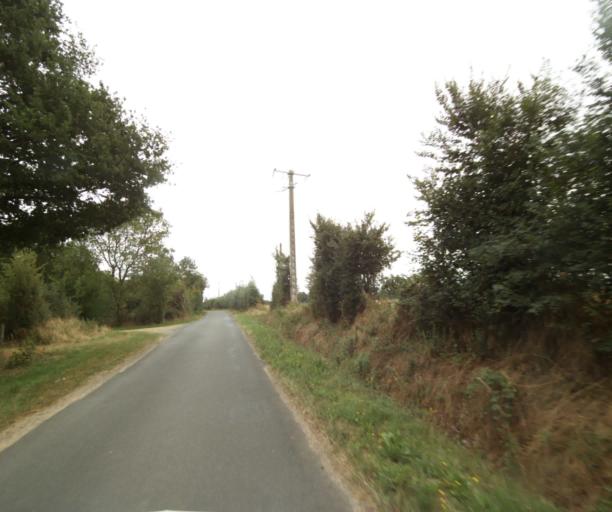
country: FR
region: Pays de la Loire
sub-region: Departement de la Sarthe
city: Vion
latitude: 47.8484
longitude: -0.2525
